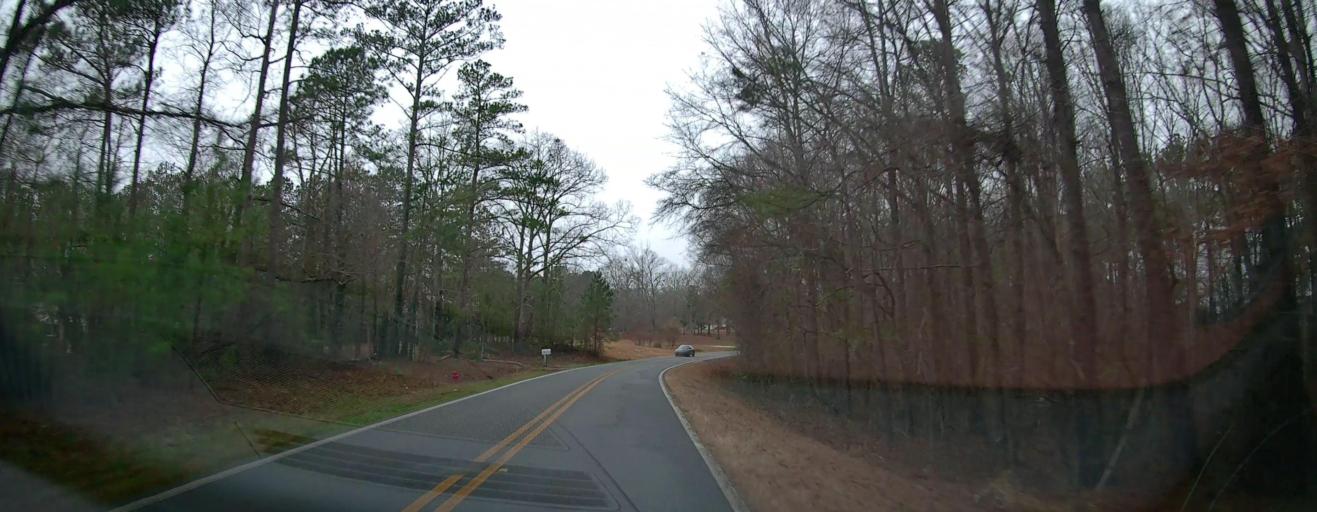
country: US
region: Georgia
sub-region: Monroe County
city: Forsyth
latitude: 33.1152
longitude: -83.9540
